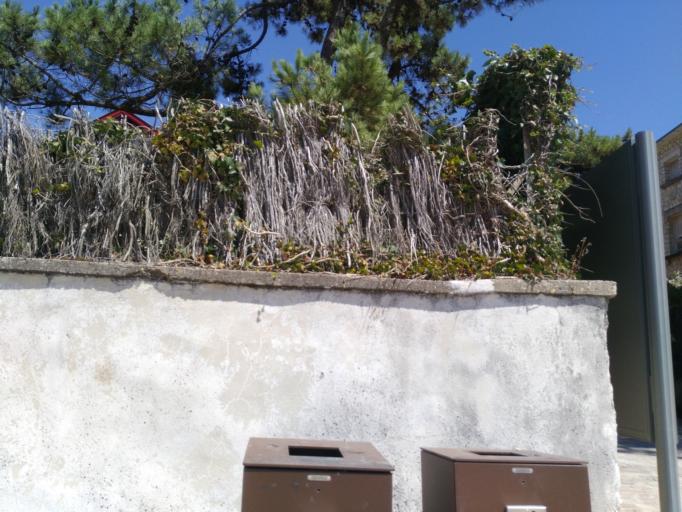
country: FR
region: Poitou-Charentes
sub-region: Departement de la Charente-Maritime
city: Saint-Palais-sur-Mer
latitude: 45.6415
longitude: -1.0868
